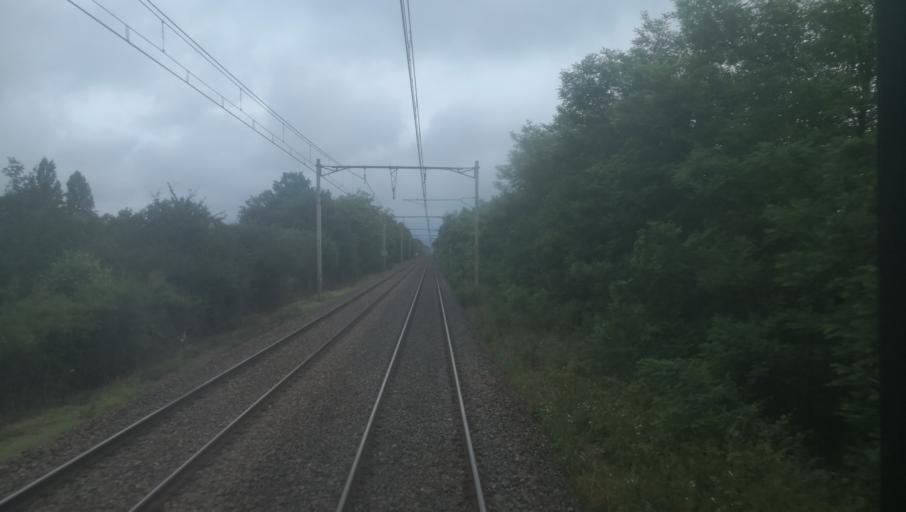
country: FR
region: Centre
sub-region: Departement du Loir-et-Cher
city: Theillay
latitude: 47.3015
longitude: 2.0434
